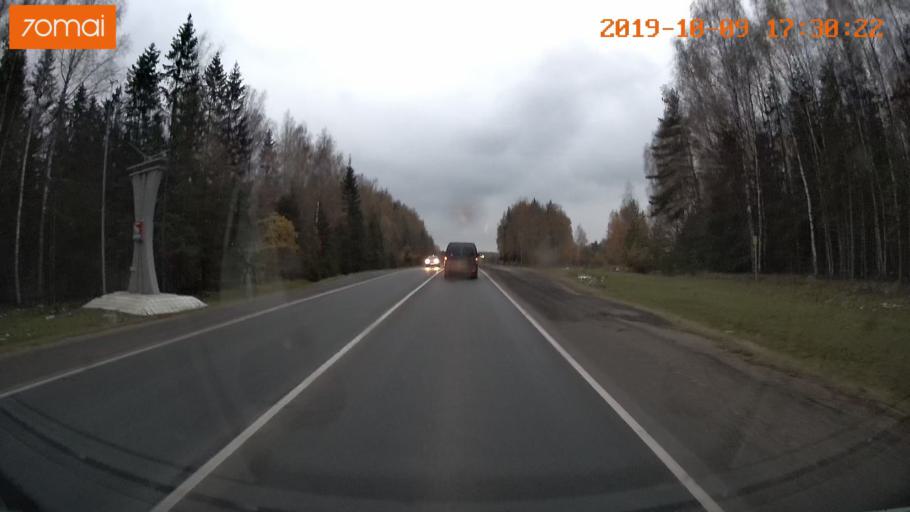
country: RU
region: Ivanovo
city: Bogorodskoye
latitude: 57.1432
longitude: 41.0500
